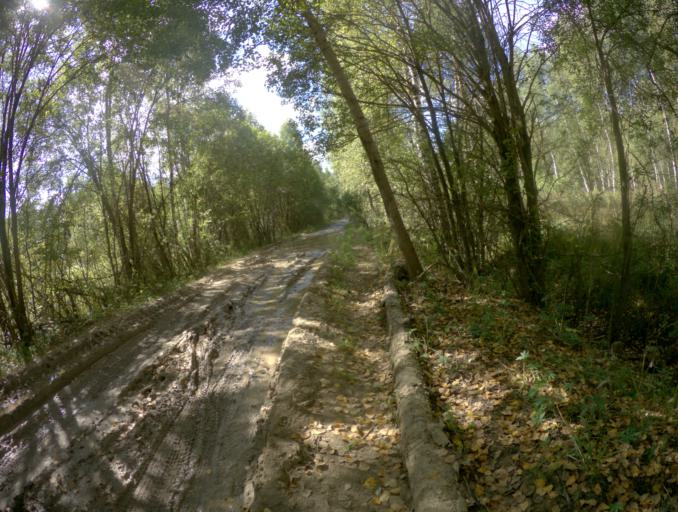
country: RU
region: Vladimir
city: Nikologory
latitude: 56.0258
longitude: 41.9429
